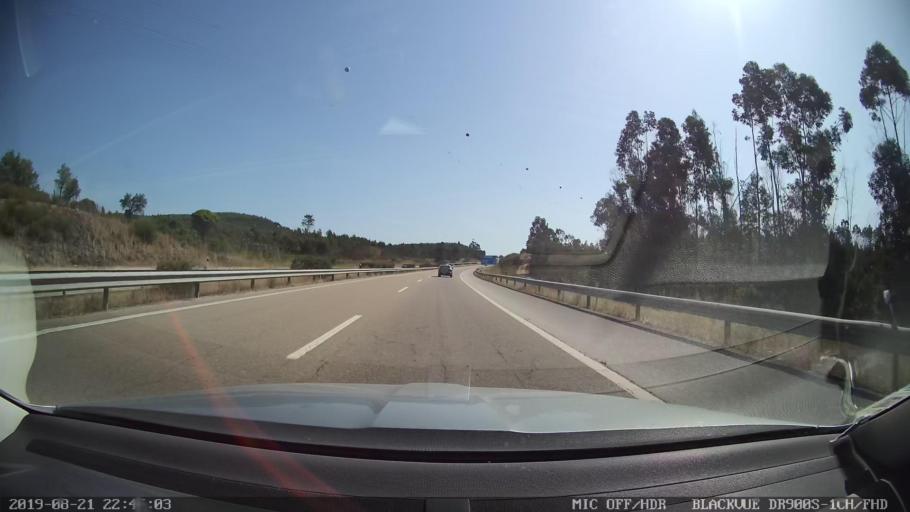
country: PT
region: Santarem
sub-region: Constancia
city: Constancia
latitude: 39.4875
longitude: -8.3219
